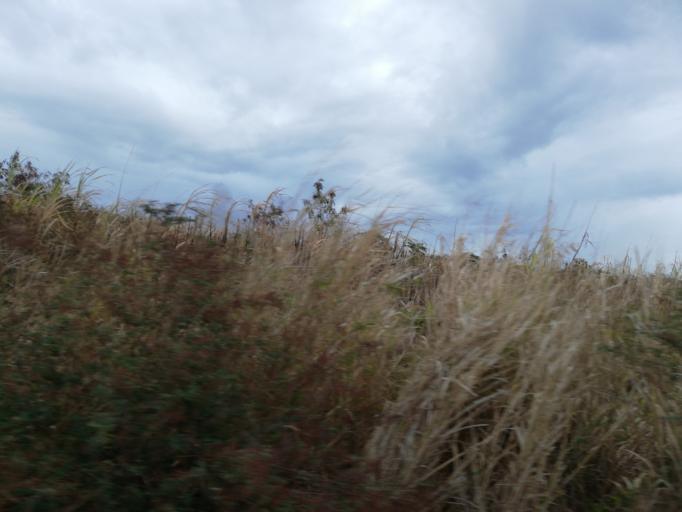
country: MU
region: Black River
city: Petite Riviere
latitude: -20.2077
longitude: 57.4583
